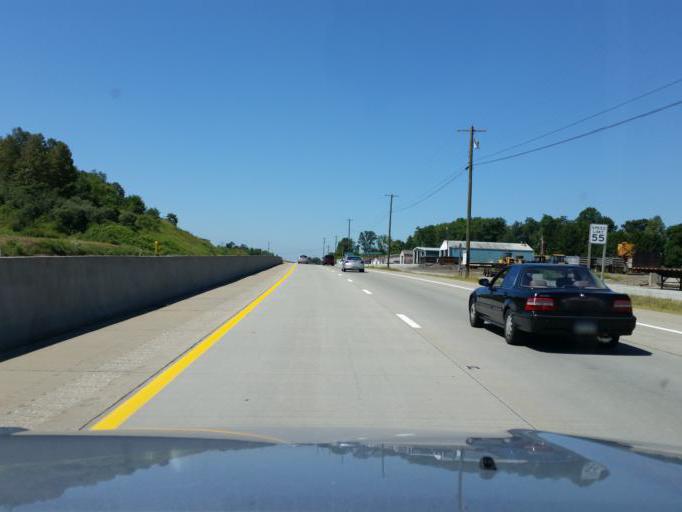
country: US
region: Pennsylvania
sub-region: Westmoreland County
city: Loyalhanna
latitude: 40.4192
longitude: -79.3657
